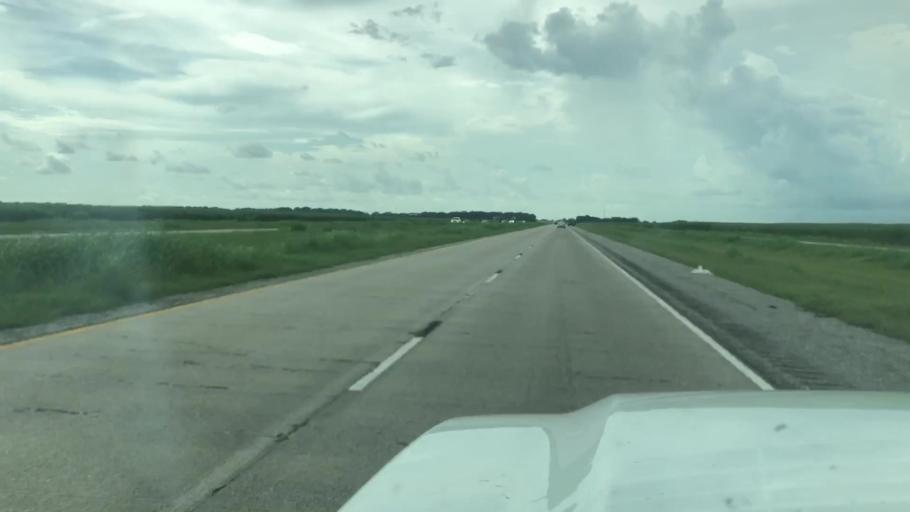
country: US
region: Louisiana
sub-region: Saint Mary Parish
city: Baldwin
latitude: 29.8483
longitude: -91.5918
